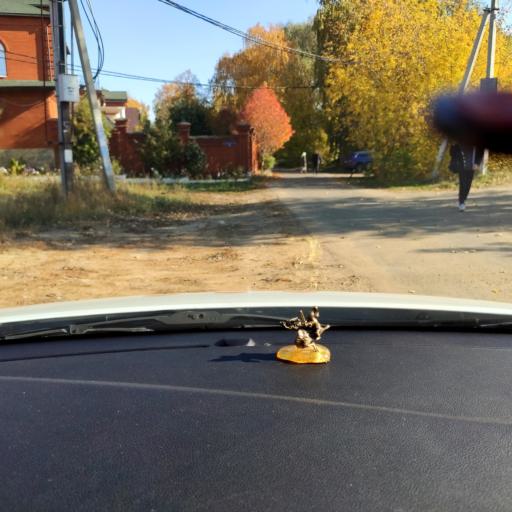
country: RU
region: Tatarstan
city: Verkhniy Uslon
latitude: 55.7997
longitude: 49.0232
